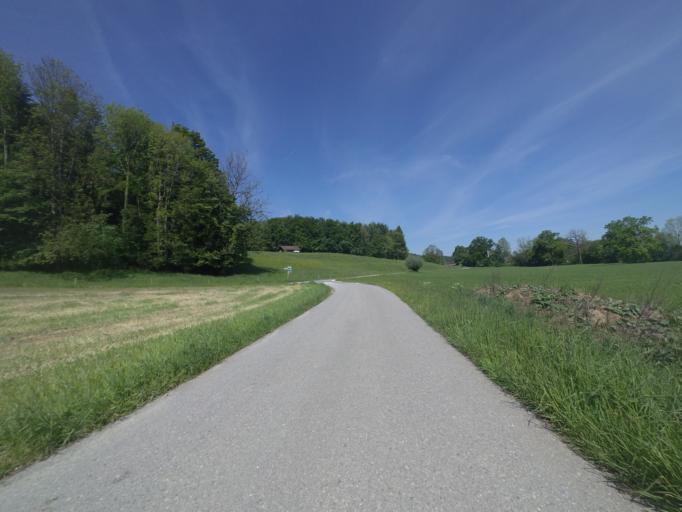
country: DE
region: Bavaria
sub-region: Upper Bavaria
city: Petting
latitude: 47.8870
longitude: 12.8302
